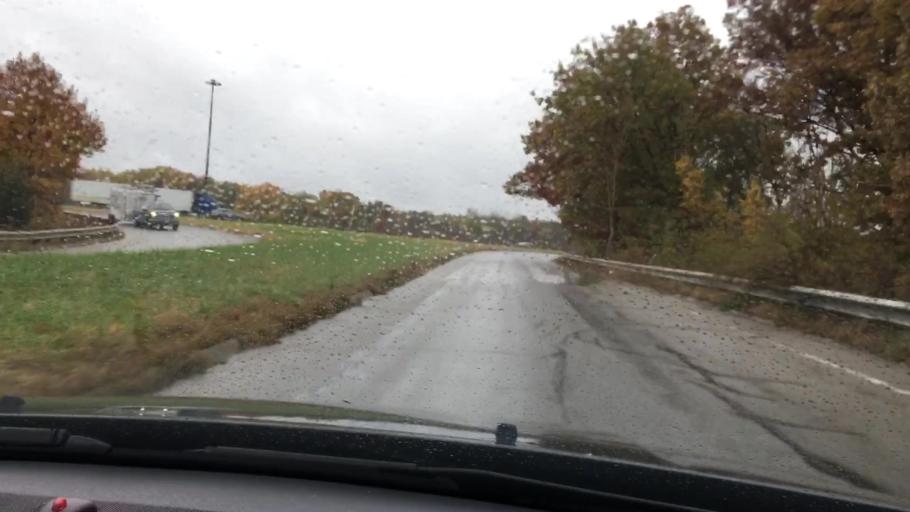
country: US
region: Massachusetts
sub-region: Middlesex County
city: Lowell
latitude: 42.6082
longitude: -71.3288
